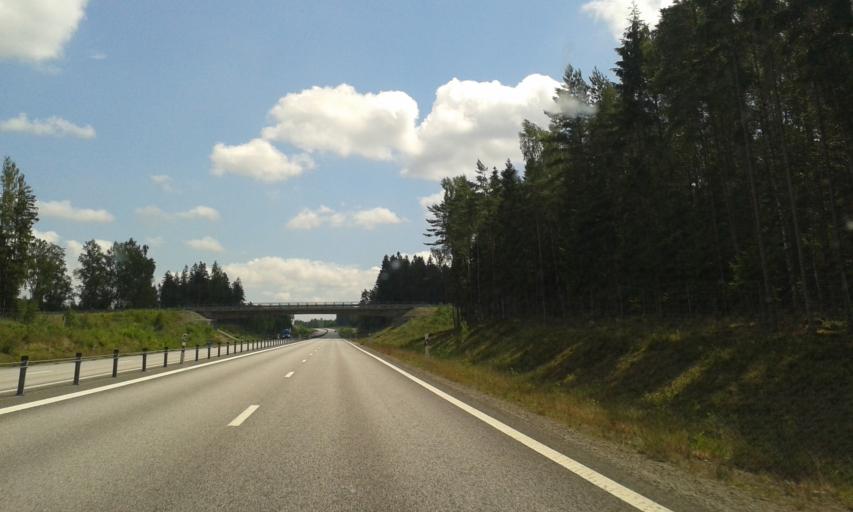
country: SE
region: Kronoberg
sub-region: Vaxjo Kommun
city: Gemla
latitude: 56.9143
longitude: 14.6261
